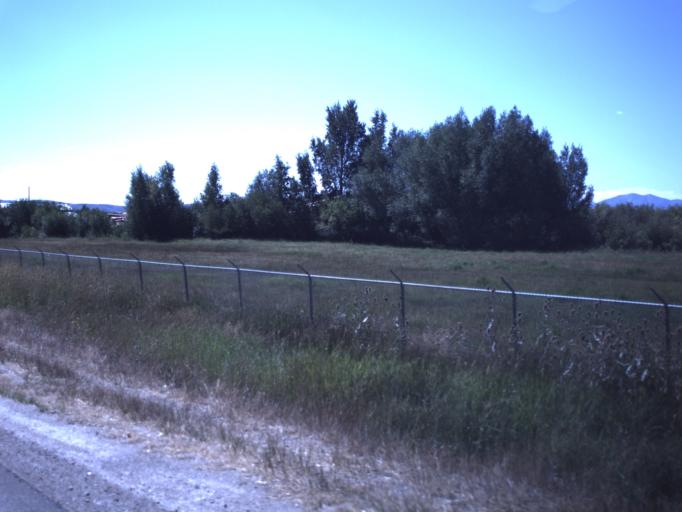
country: US
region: Utah
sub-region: Summit County
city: Kamas
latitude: 40.6541
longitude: -111.2808
